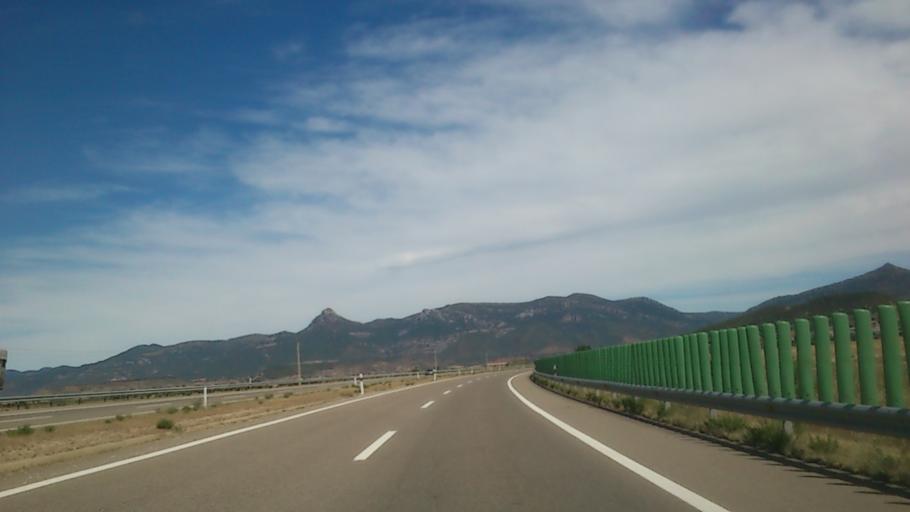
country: ES
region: Aragon
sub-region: Provincia de Huesca
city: Igries
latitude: 42.1940
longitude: -0.4356
